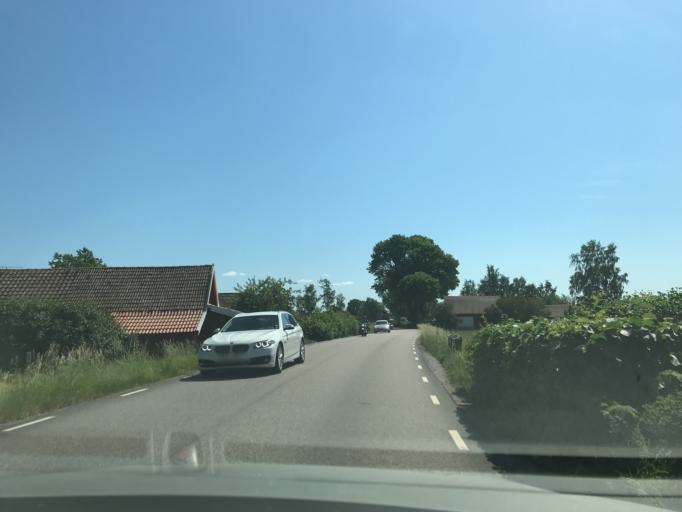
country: SE
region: Vaestra Goetaland
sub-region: Gotene Kommun
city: Kallby
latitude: 58.5235
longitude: 13.3217
